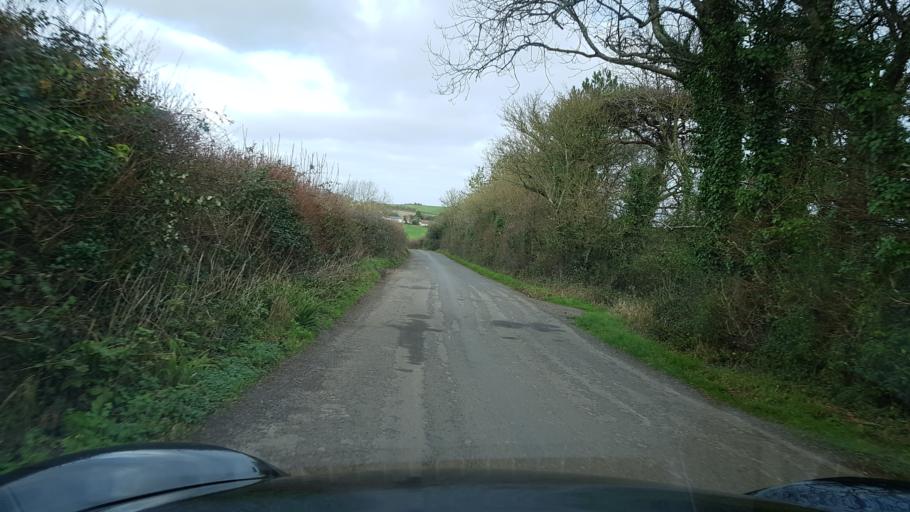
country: GB
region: England
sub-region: Dorset
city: Bridport
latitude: 50.7154
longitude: -2.7157
